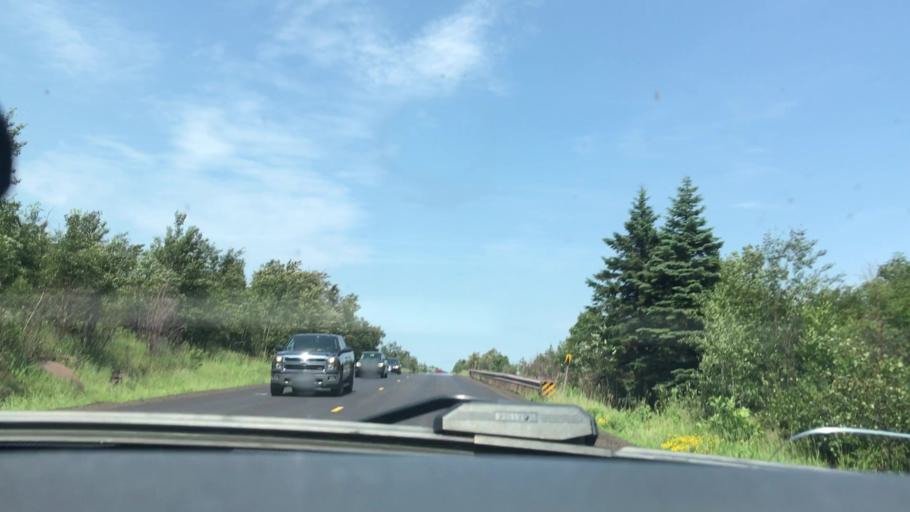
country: US
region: Minnesota
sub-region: Lake County
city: Silver Bay
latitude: 47.2803
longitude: -91.2708
